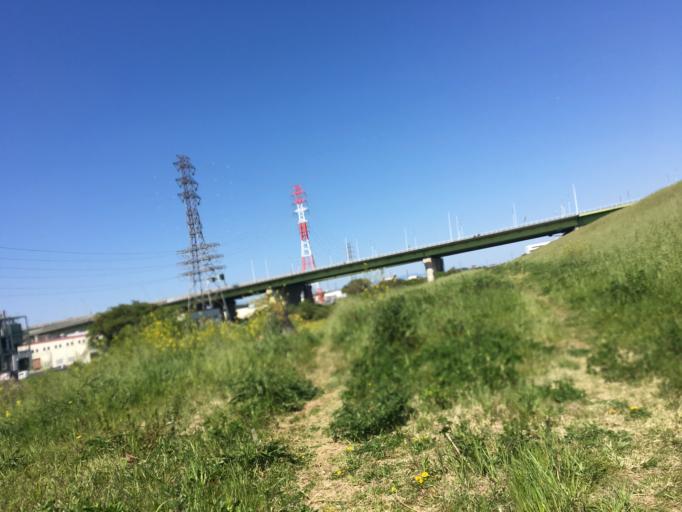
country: JP
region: Saitama
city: Wako
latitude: 35.8055
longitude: 139.6272
